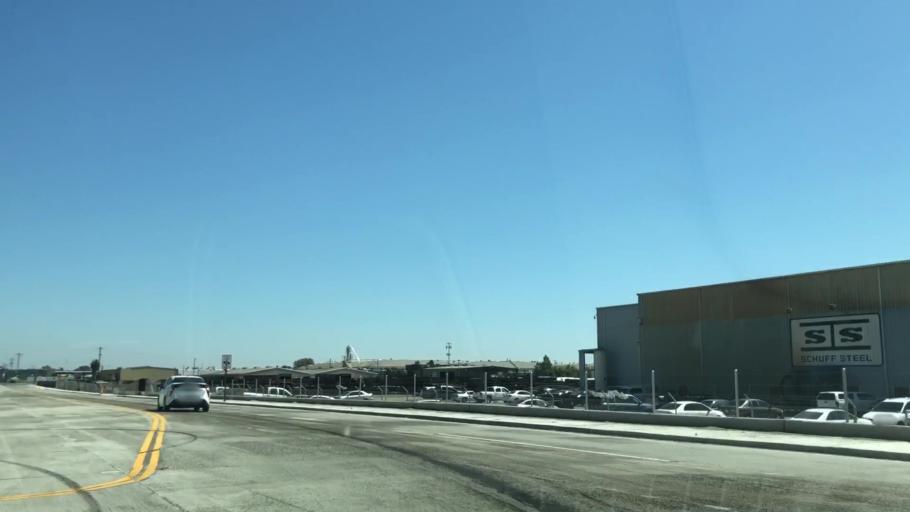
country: US
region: California
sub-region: San Joaquin County
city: Country Club
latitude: 37.9375
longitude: -121.3226
